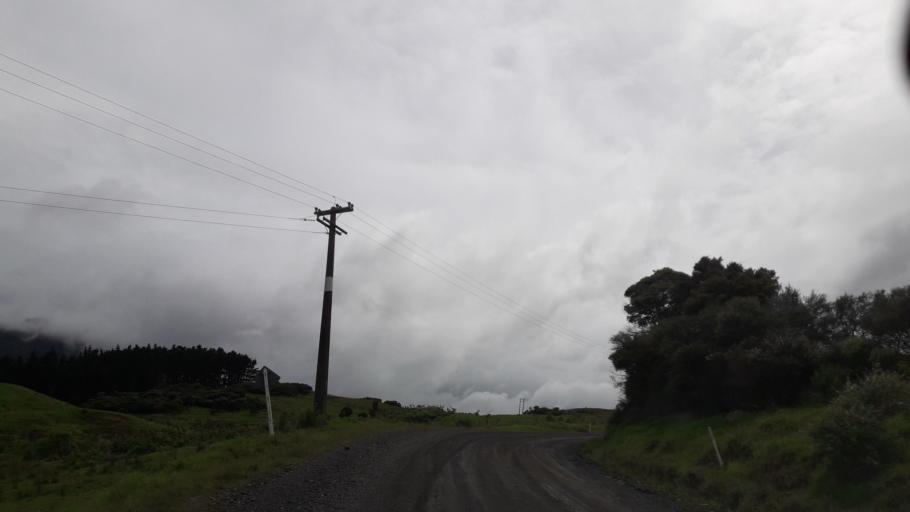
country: NZ
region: Northland
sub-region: Far North District
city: Kaitaia
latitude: -35.4160
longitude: 173.3646
